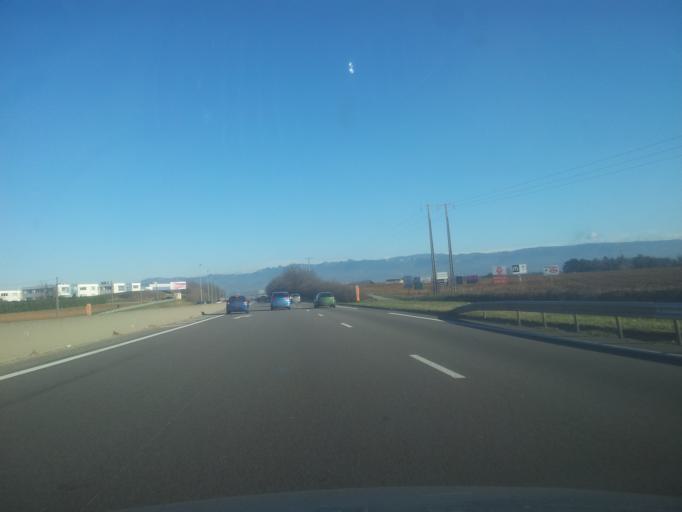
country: FR
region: Rhone-Alpes
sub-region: Departement de la Drome
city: Valence
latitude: 44.9018
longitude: 4.9003
